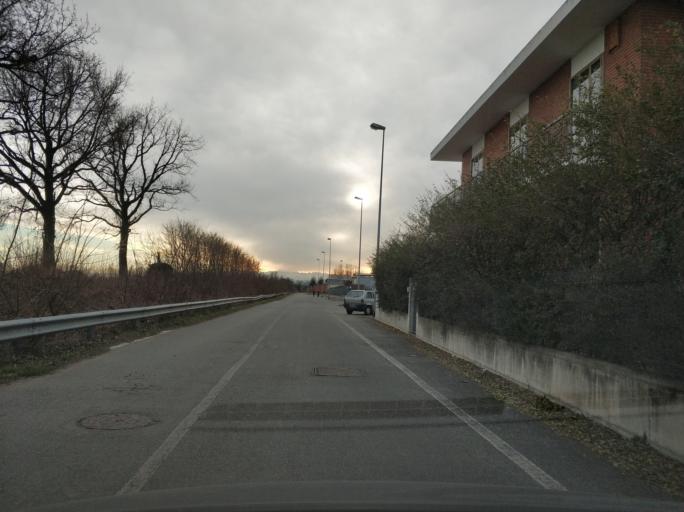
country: IT
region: Piedmont
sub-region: Provincia di Torino
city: Caselle Torinese
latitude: 45.1924
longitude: 7.6262
